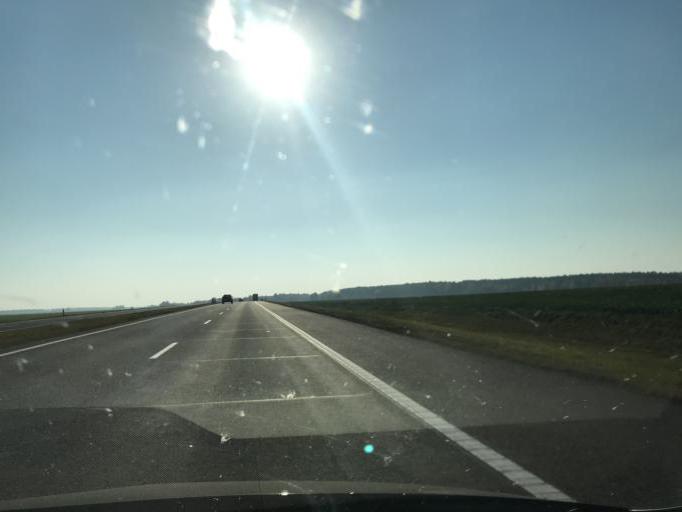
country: BY
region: Grodnenskaya
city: Mir
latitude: 53.4263
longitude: 26.5808
